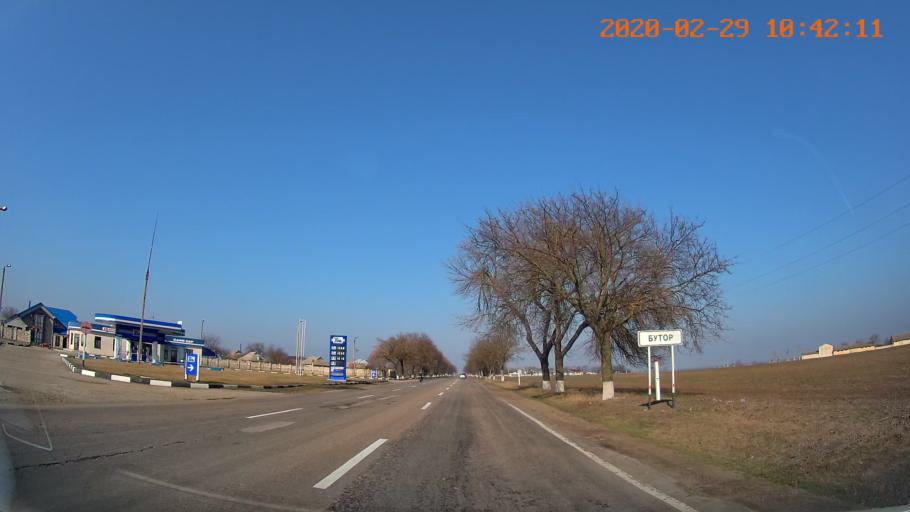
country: MD
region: Telenesti
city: Grigoriopol
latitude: 47.0494
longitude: 29.4144
